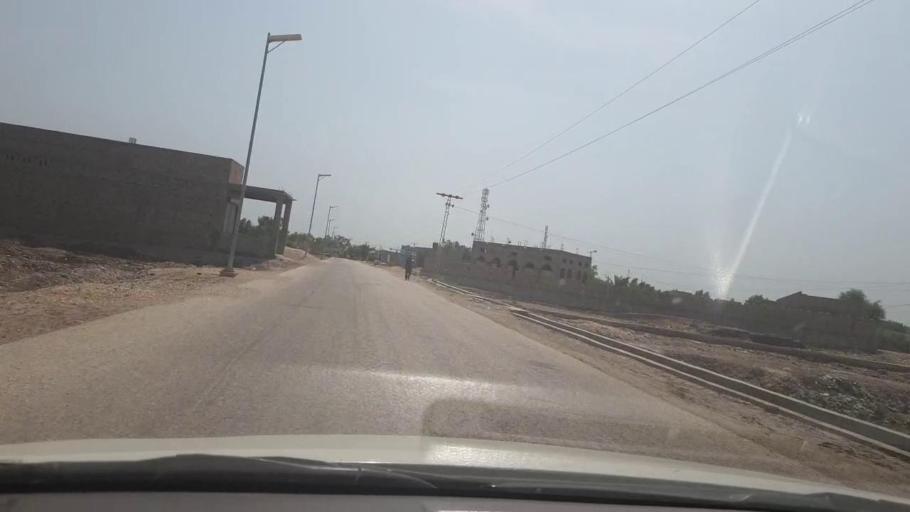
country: PK
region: Sindh
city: Garhi Yasin
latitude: 27.9124
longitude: 68.5171
